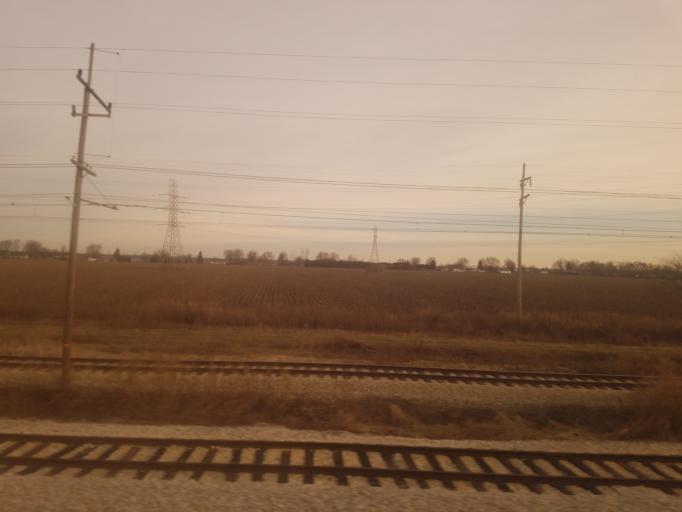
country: US
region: Indiana
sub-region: Saint Joseph County
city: New Carlisle
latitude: 41.7020
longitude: -86.4640
